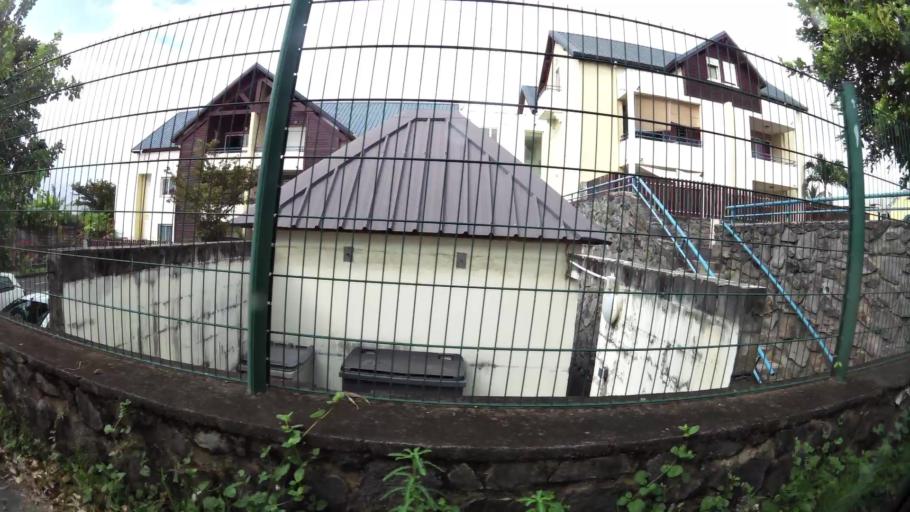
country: RE
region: Reunion
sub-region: Reunion
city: Sainte-Marie
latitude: -20.8967
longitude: 55.5713
